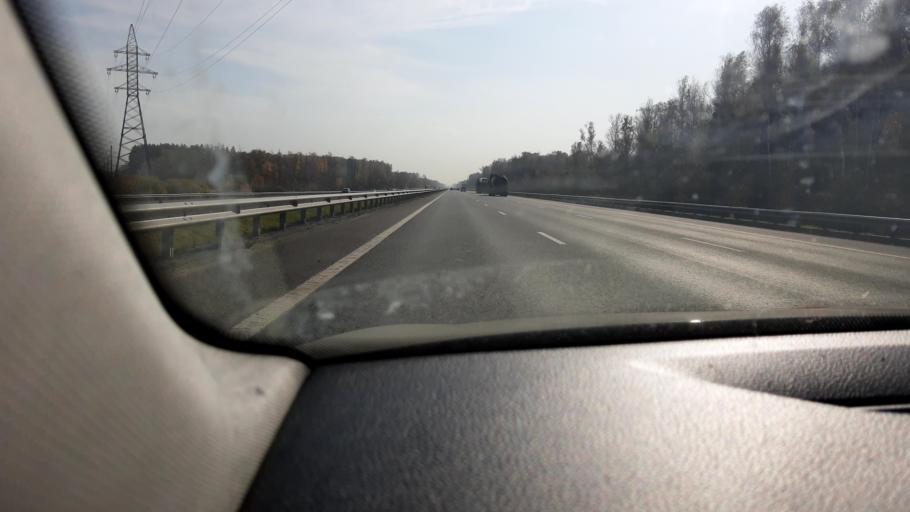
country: RU
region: Moskovskaya
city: Zhilevo
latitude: 54.9534
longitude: 37.9829
